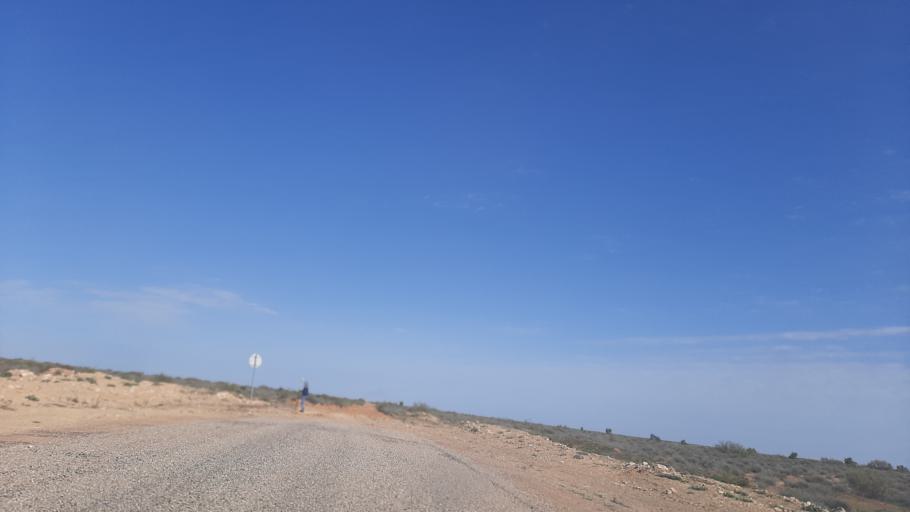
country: TN
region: Madanin
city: Medenine
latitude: 33.2429
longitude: 10.7406
